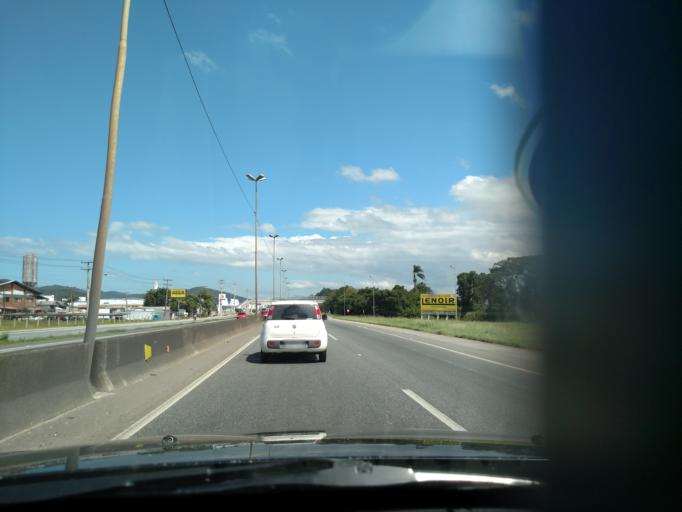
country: BR
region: Santa Catarina
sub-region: Itajai
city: Itajai
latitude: -26.9191
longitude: -48.7094
